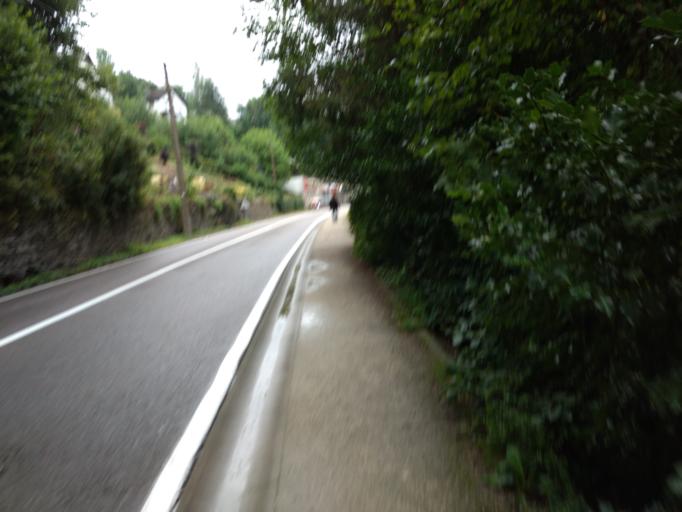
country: BE
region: Wallonia
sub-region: Province du Luxembourg
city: La Roche-en-Ardenne
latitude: 50.1813
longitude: 5.5836
